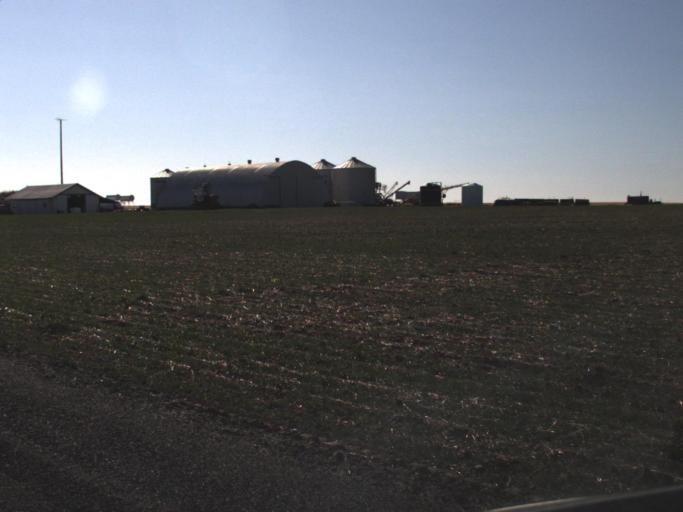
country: US
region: Washington
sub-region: Franklin County
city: Connell
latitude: 46.8119
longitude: -118.5473
